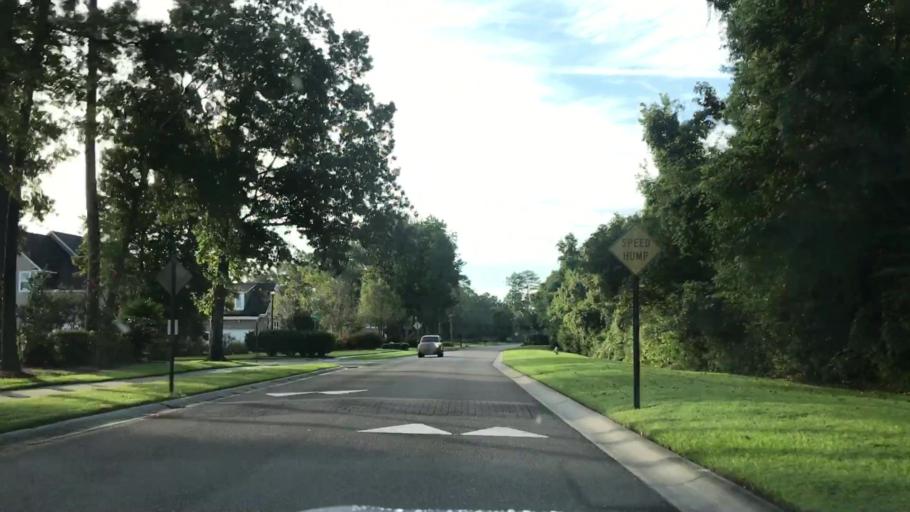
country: US
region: South Carolina
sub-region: Charleston County
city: Shell Point
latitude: 32.8390
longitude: -80.0739
